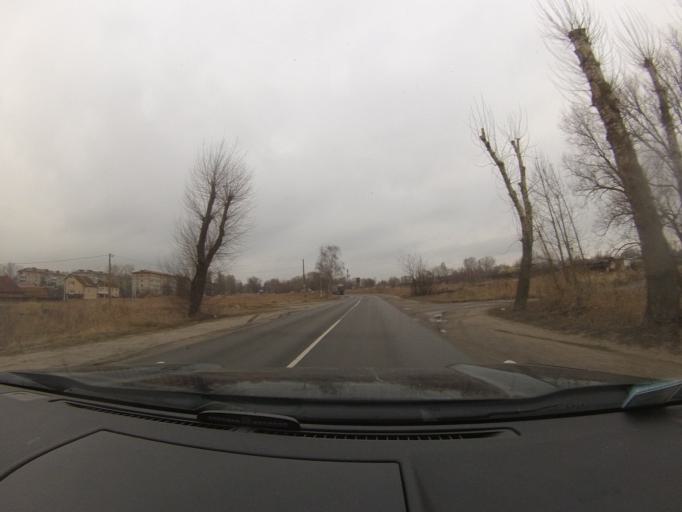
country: RU
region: Moskovskaya
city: Lopatinskiy
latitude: 55.3353
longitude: 38.7279
